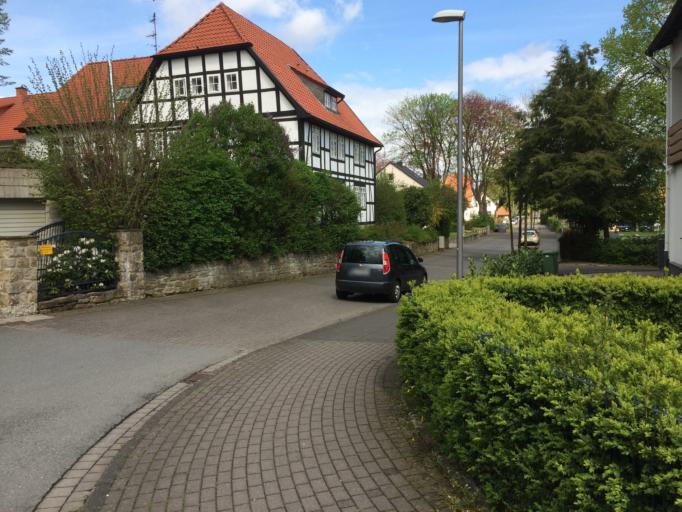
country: DE
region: North Rhine-Westphalia
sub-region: Regierungsbezirk Detmold
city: Detmold
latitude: 51.9211
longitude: 8.8449
